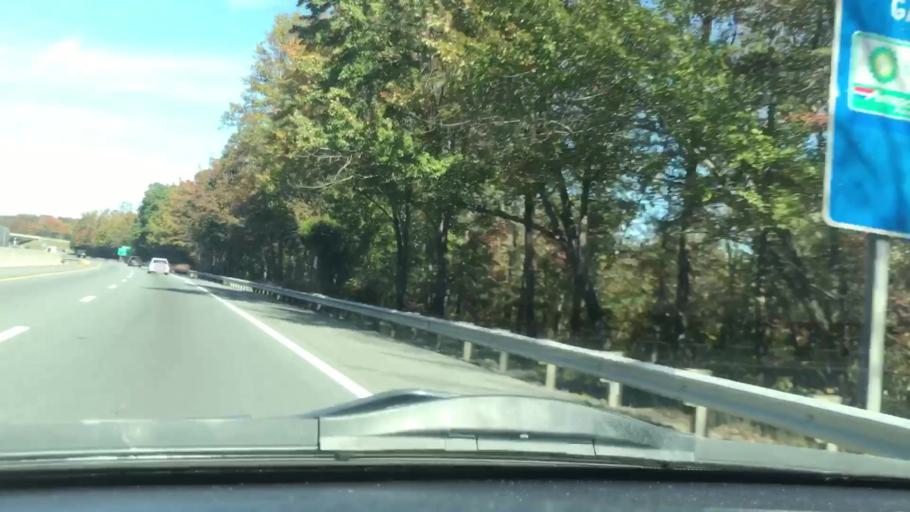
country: US
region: North Carolina
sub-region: Randolph County
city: Asheboro
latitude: 35.7265
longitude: -79.8242
